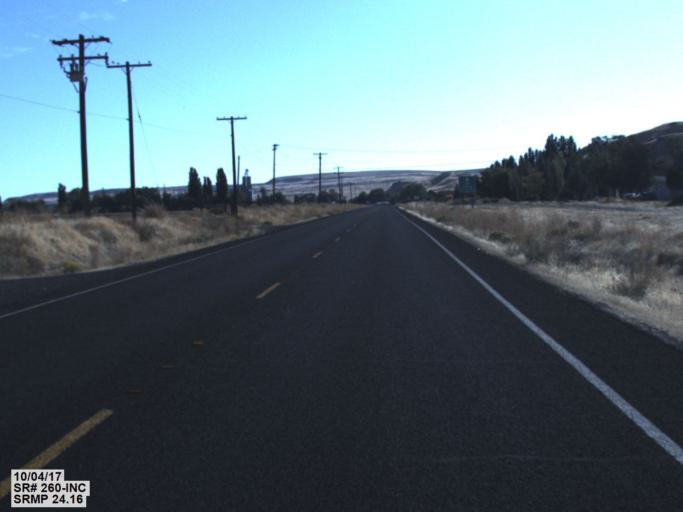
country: US
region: Washington
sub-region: Franklin County
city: Connell
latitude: 46.6440
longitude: -118.5698
